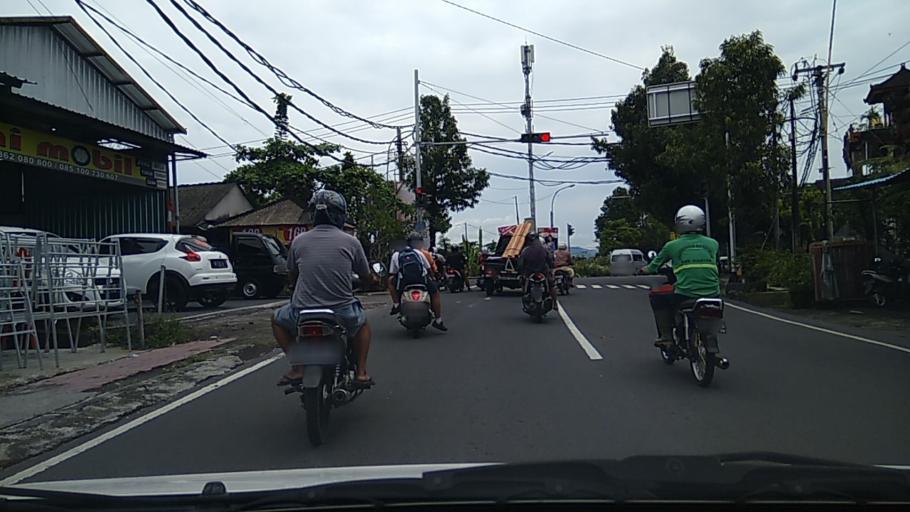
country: ID
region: Bali
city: Banjar Kelodan
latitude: -8.5403
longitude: 115.3373
